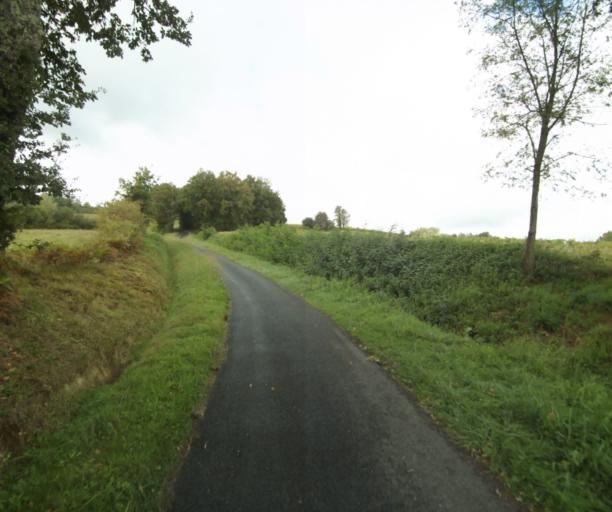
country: FR
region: Midi-Pyrenees
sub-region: Departement du Gers
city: Nogaro
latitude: 43.8270
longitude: -0.0906
